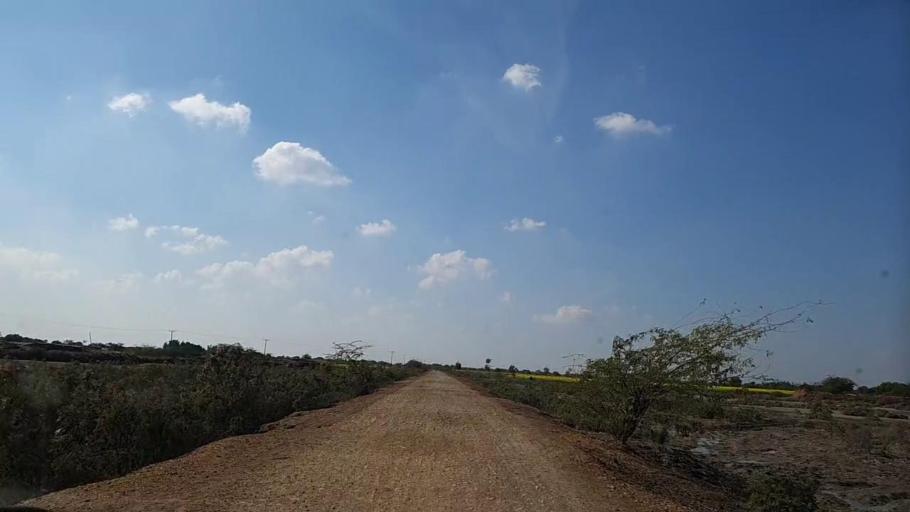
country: PK
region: Sindh
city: Pithoro
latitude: 25.6141
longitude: 69.4063
